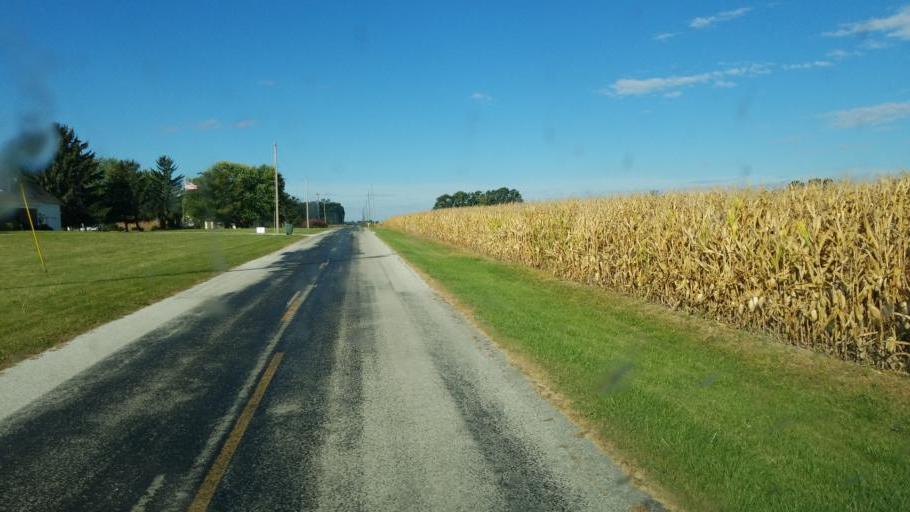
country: US
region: Ohio
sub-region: Marion County
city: Marion
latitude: 40.6884
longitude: -83.0788
